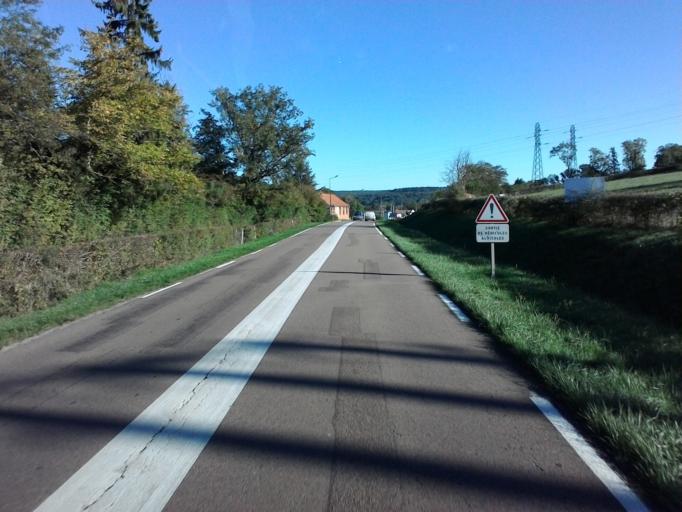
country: FR
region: Bourgogne
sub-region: Departement de la Cote-d'Or
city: Montbard
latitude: 47.6130
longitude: 4.3162
